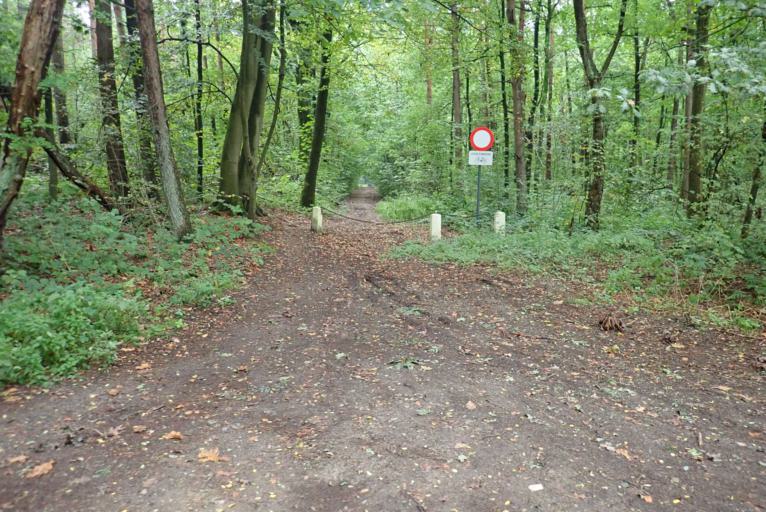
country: BE
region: Flanders
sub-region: Provincie Antwerpen
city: Grobbendonk
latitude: 51.2035
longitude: 4.7466
